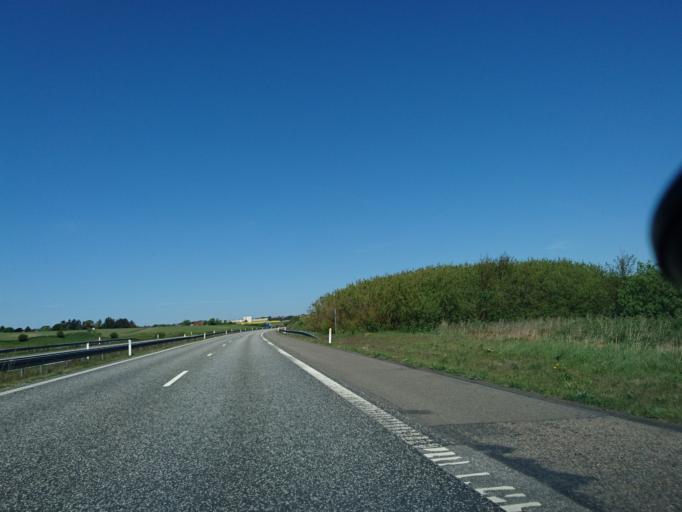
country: DK
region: North Denmark
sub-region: Hjorring Kommune
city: Hirtshals
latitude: 57.5365
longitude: 10.0087
